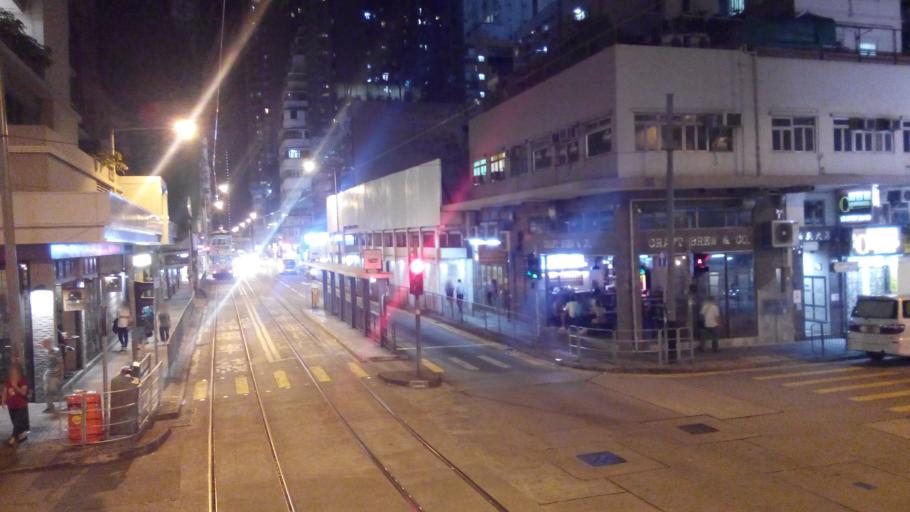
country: HK
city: Hong Kong
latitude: 22.2833
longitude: 114.1295
